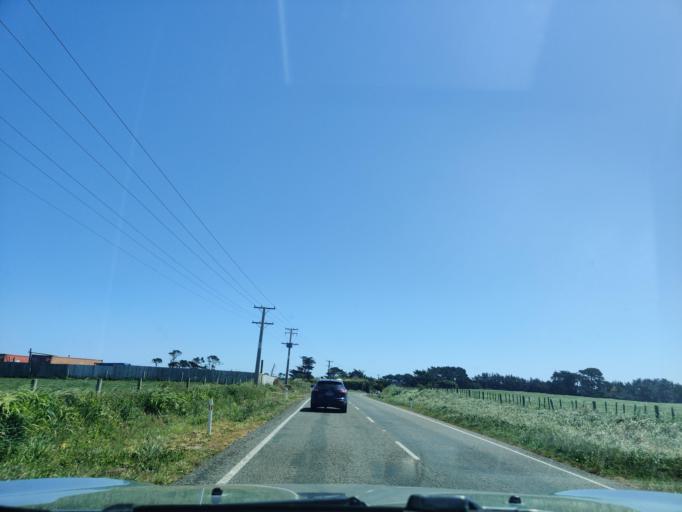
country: NZ
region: Taranaki
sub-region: South Taranaki District
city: Hawera
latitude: -39.5458
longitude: 174.0768
